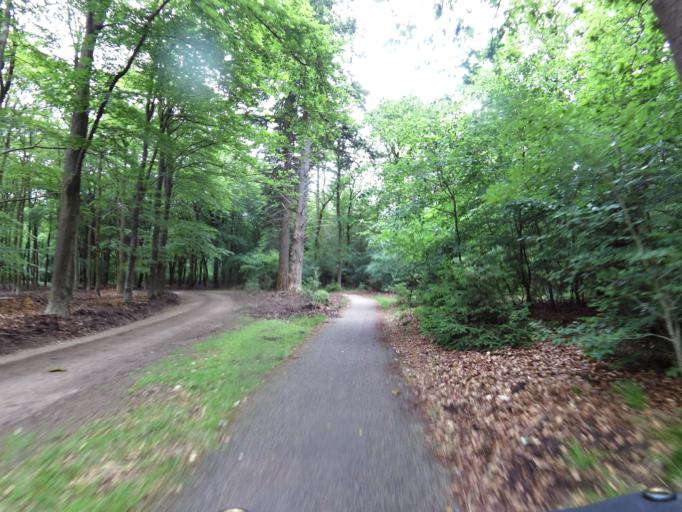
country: NL
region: Gelderland
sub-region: Gemeente Apeldoorn
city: Uddel
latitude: 52.2870
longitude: 5.8044
